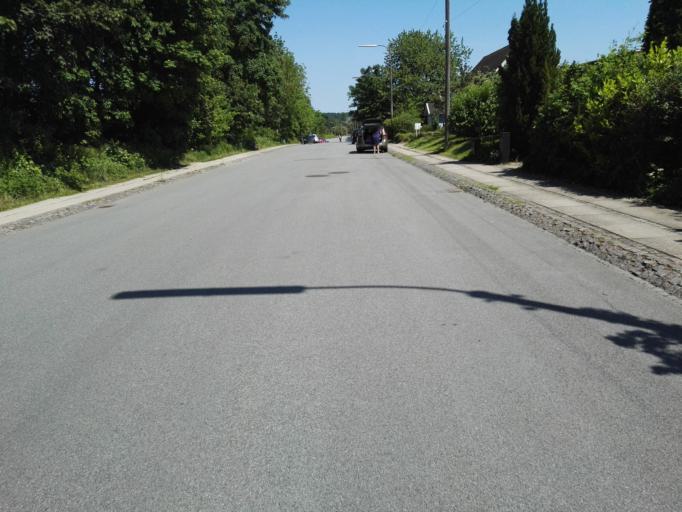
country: DK
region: Capital Region
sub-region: Fureso Kommune
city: Vaerlose
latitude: 55.7551
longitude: 12.3870
